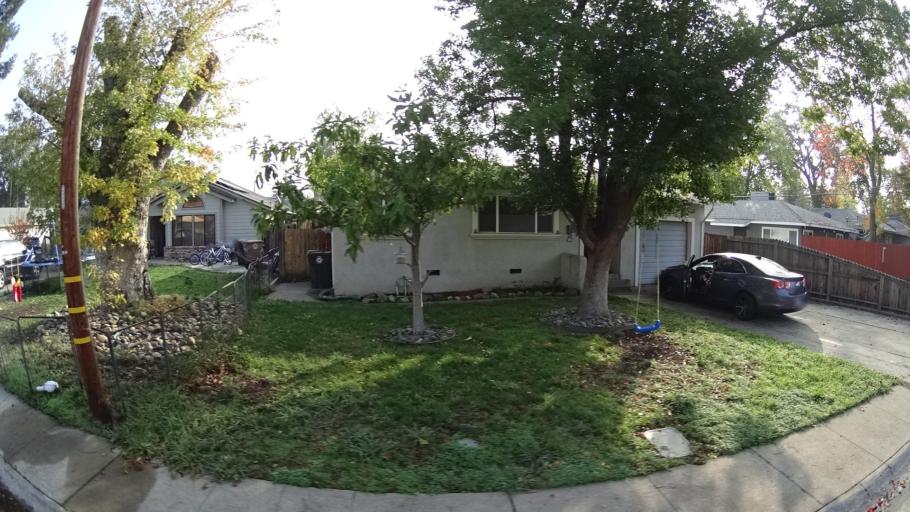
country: US
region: California
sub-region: Sacramento County
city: Elk Grove
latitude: 38.4061
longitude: -121.3582
